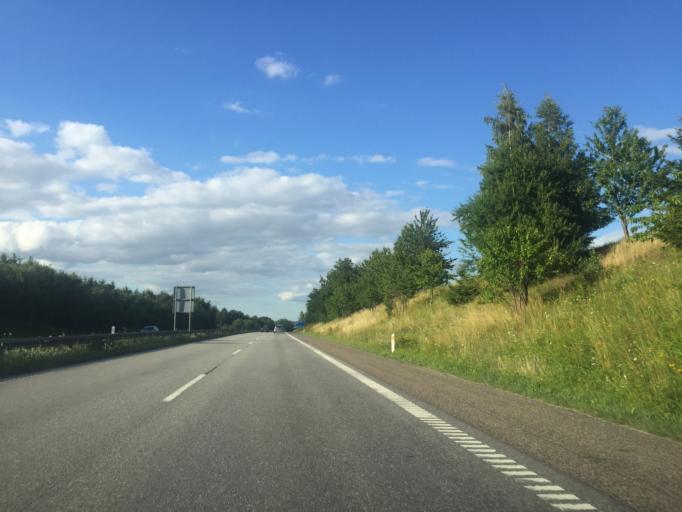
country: DK
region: Zealand
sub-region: Faxe Kommune
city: Ronnede
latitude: 55.2452
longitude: 11.9864
